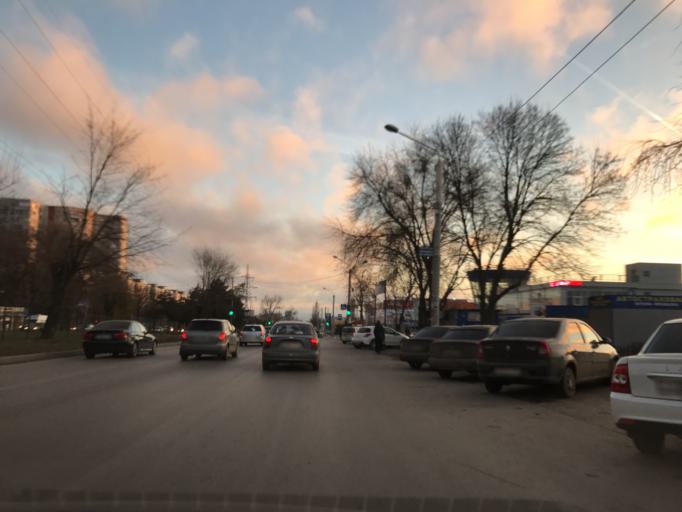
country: RU
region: Rostov
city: Kalinin
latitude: 47.2338
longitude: 39.6134
